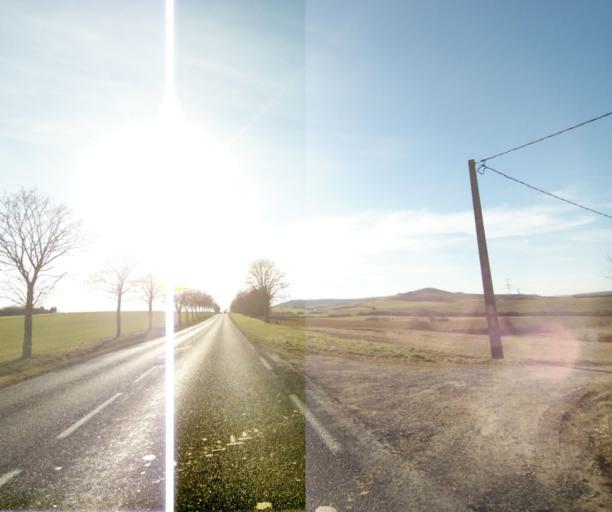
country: FR
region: Lorraine
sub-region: Departement de Meurthe-et-Moselle
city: Seichamps
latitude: 48.7258
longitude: 6.2819
